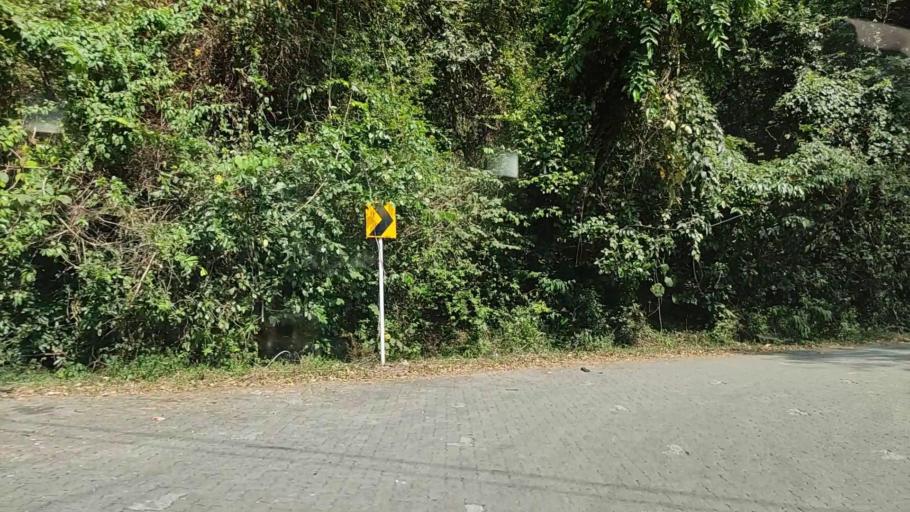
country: IN
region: Kerala
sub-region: Kollam
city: Punalur
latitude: 8.9610
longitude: 77.0672
